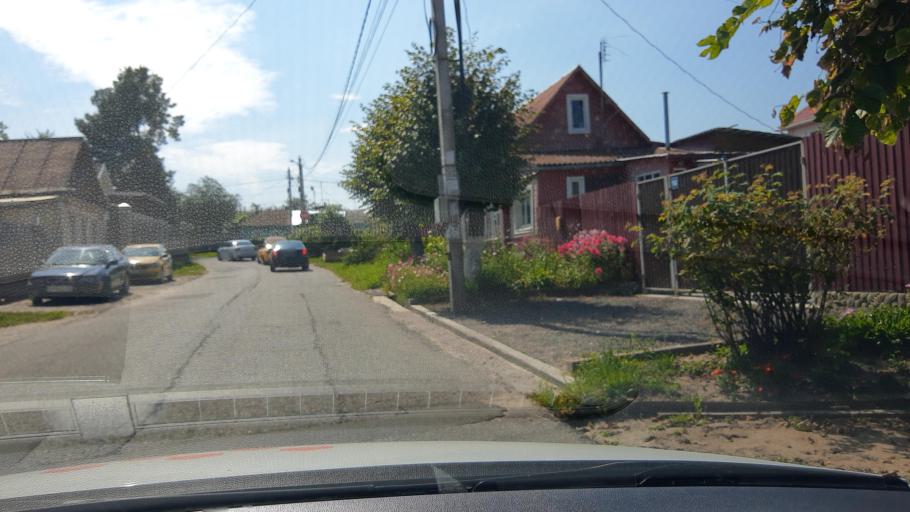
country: RU
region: Moskovskaya
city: Bronnitsy
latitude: 55.4270
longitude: 38.2553
